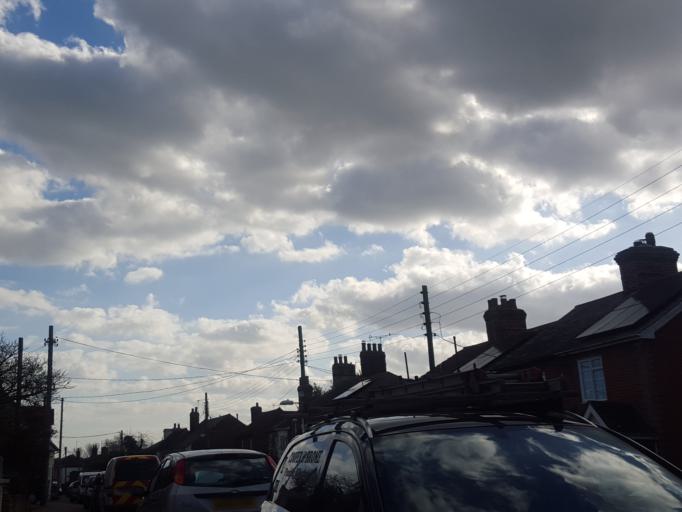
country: GB
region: England
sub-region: Essex
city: Little Clacton
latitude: 51.8579
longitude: 1.1164
